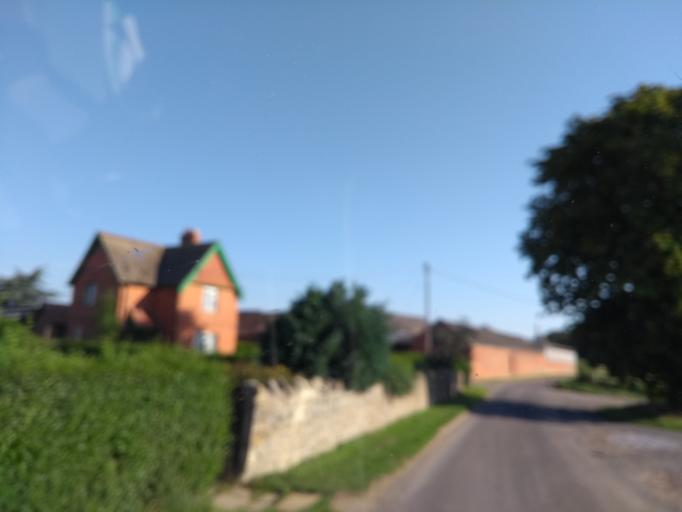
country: GB
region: England
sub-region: Somerset
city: Westonzoyland
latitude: 51.1242
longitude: -2.9479
